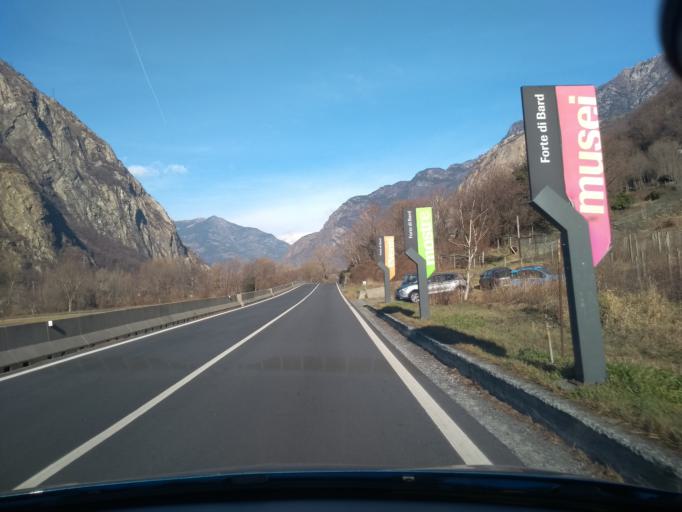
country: IT
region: Aosta Valley
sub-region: Valle d'Aosta
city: Hone
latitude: 45.6194
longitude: 7.7393
